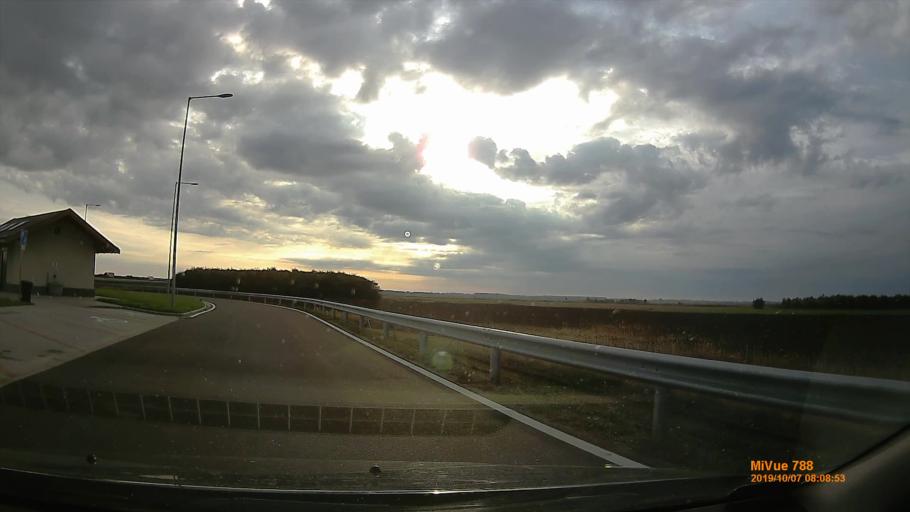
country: HU
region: Jasz-Nagykun-Szolnok
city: Cserkeszolo
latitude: 46.8836
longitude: 20.2150
